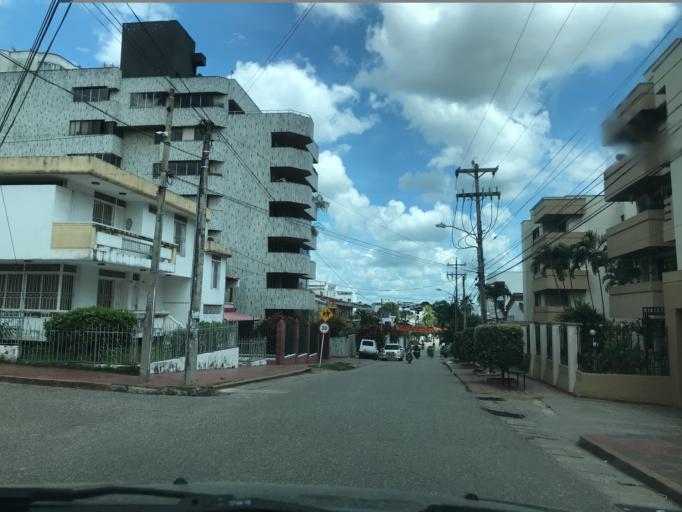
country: CO
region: Sucre
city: Sincelejo
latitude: 9.3080
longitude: -75.3977
